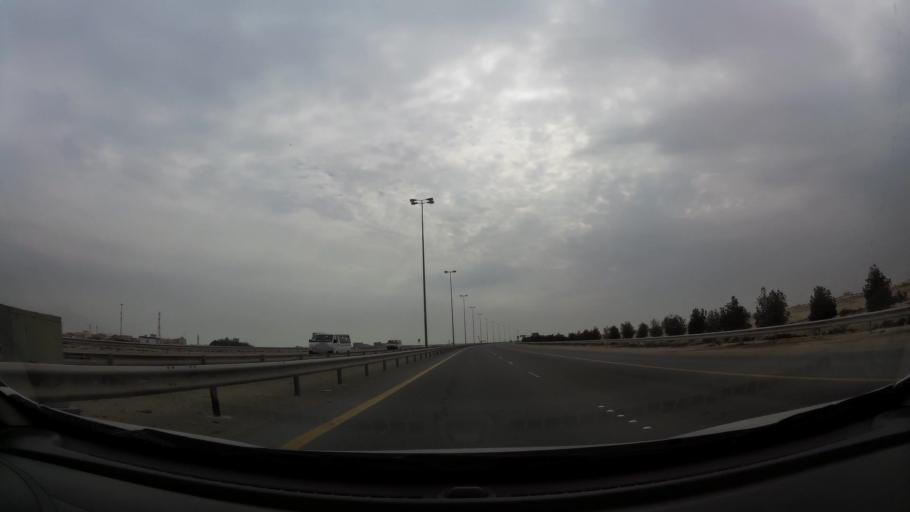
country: BH
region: Northern
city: Ar Rifa'
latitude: 26.0643
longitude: 50.6123
